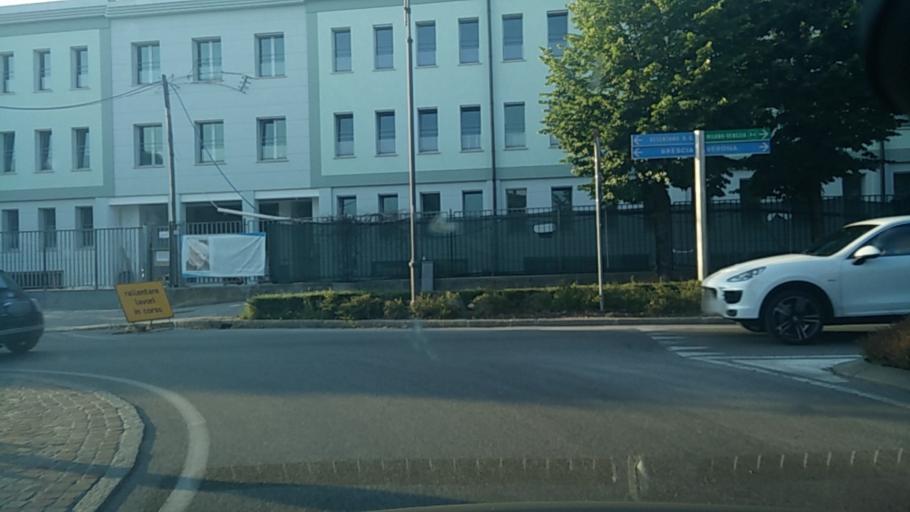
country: IT
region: Lombardy
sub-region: Provincia di Brescia
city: Desenzano del Garda
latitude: 45.4607
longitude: 10.5657
